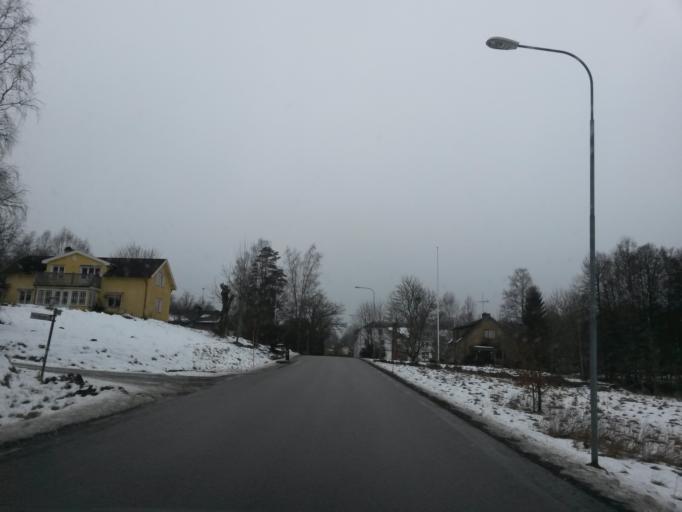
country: SE
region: Vaestra Goetaland
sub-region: Tranemo Kommun
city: Langhem
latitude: 57.6968
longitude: 13.3024
